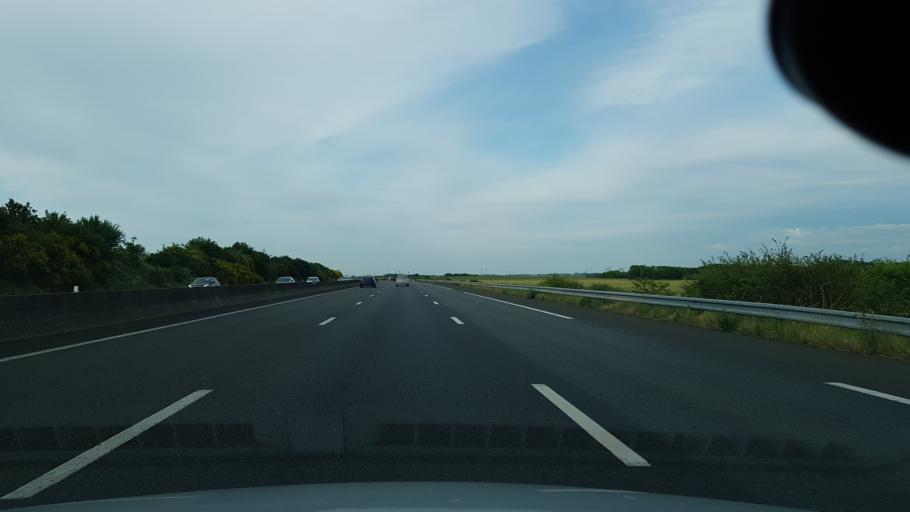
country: FR
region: Centre
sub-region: Departement du Loir-et-Cher
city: Suevres
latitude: 47.6875
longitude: 1.4243
